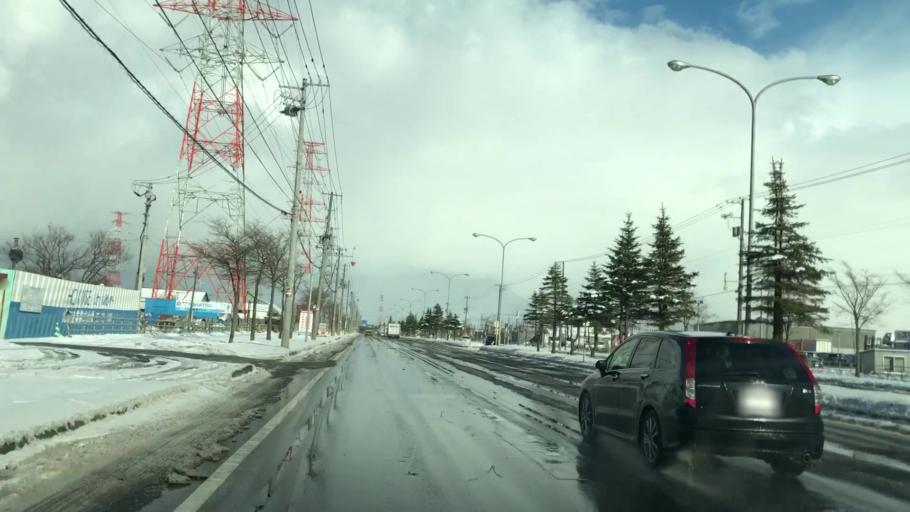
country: JP
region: Hokkaido
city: Sapporo
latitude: 43.1458
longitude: 141.4119
